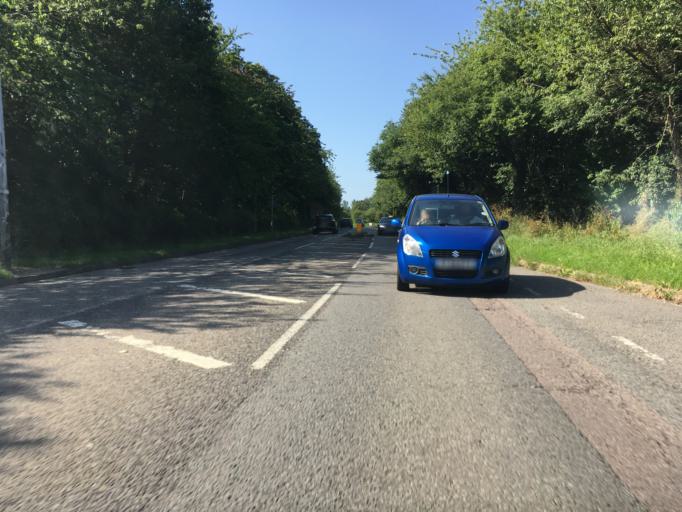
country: GB
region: England
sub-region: Milton Keynes
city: Simpson
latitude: 52.0208
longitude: -0.7019
